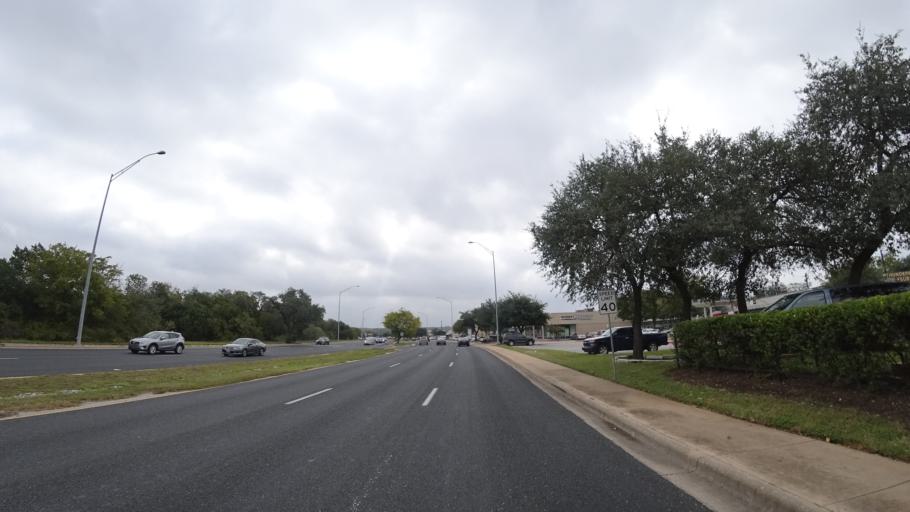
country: US
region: Texas
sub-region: Travis County
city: Shady Hollow
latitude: 30.2162
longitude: -97.8338
